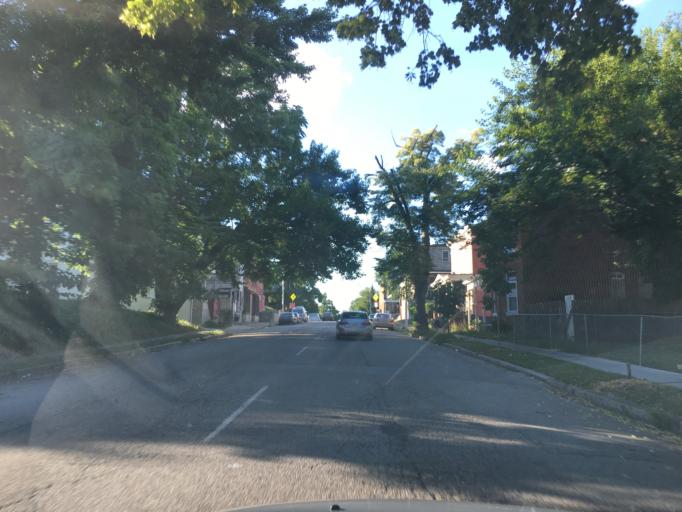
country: US
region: Maryland
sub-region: City of Baltimore
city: Baltimore
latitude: 39.3102
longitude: -76.6658
